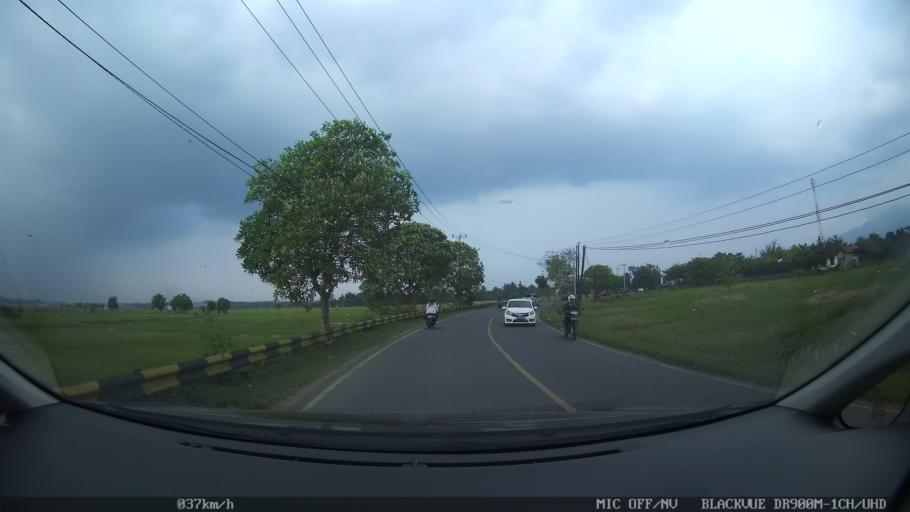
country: ID
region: Lampung
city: Gadingrejo
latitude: -5.3712
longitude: 105.0729
